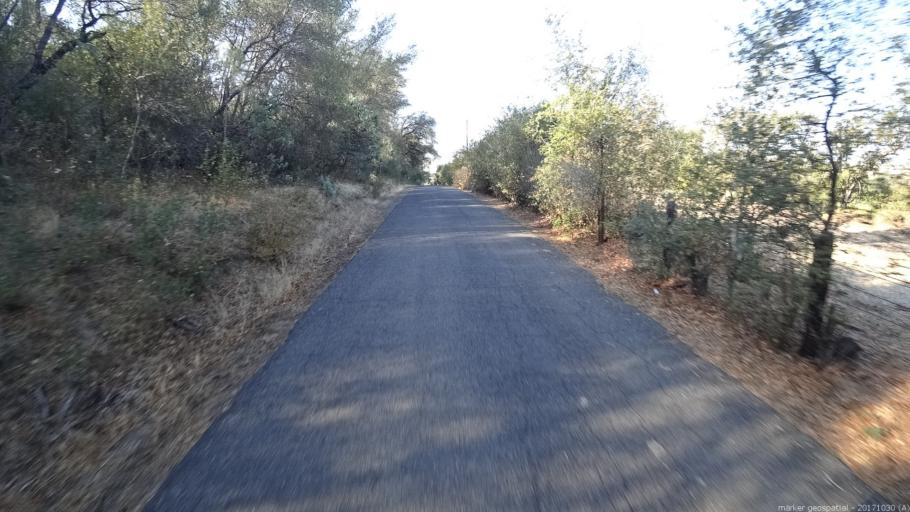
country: US
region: California
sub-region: Shasta County
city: Palo Cedro
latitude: 40.5642
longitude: -122.1522
